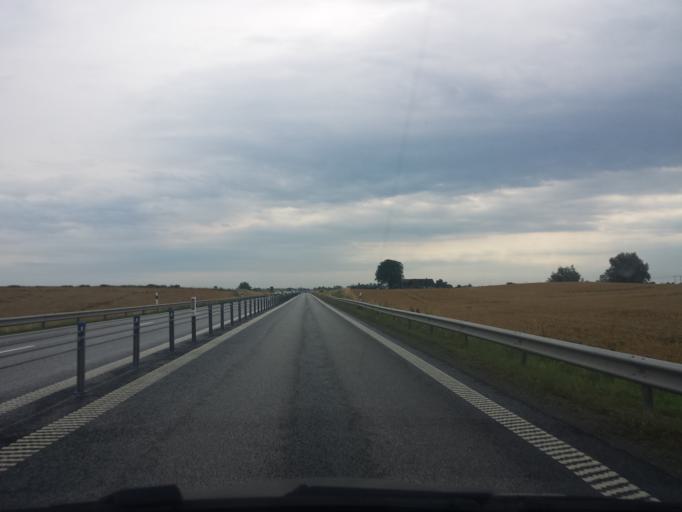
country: SE
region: Skane
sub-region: Skurups Kommun
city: Rydsgard
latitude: 55.4862
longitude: 13.5624
